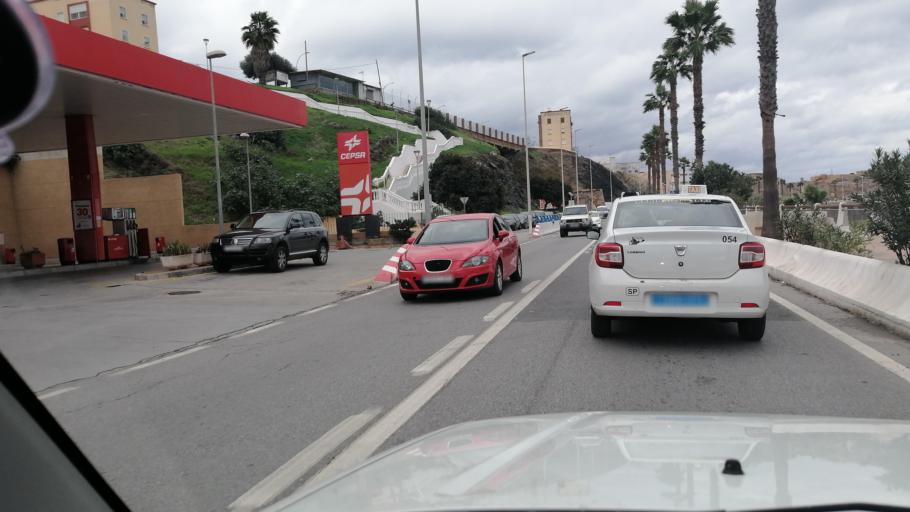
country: ES
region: Ceuta
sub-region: Ceuta
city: Ceuta
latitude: 35.8852
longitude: -5.3227
